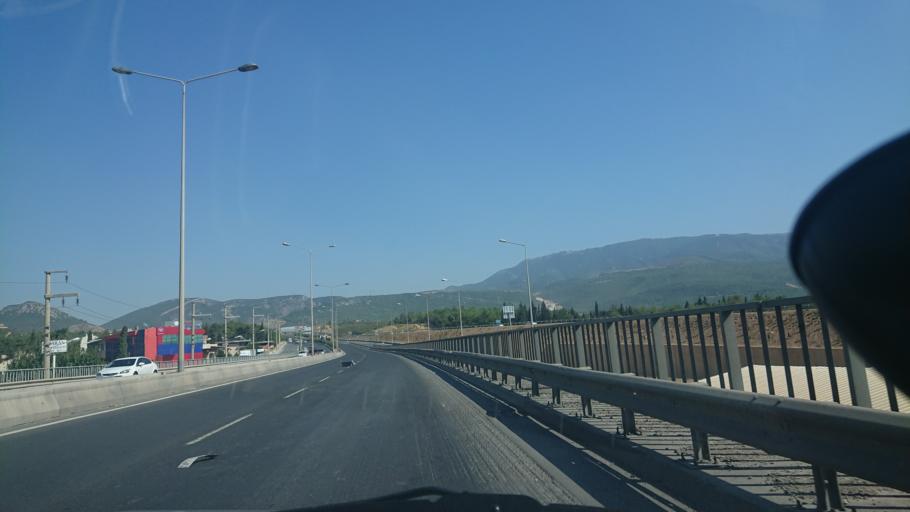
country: TR
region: Izmir
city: Bornova
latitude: 38.4521
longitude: 27.2669
